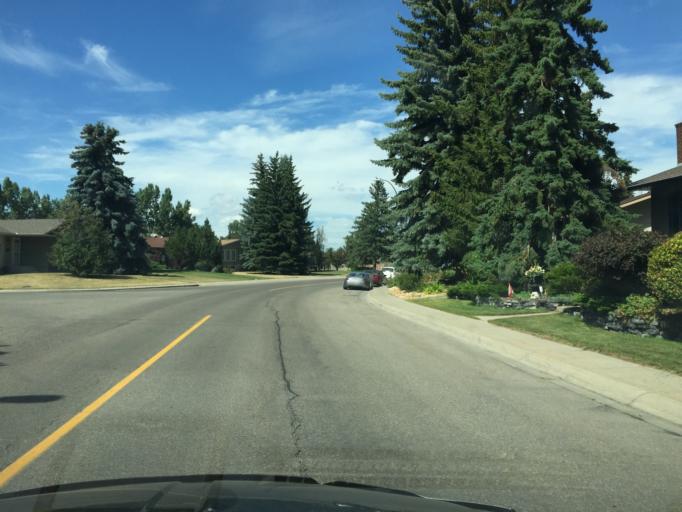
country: CA
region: Alberta
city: Calgary
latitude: 50.9461
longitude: -114.0656
